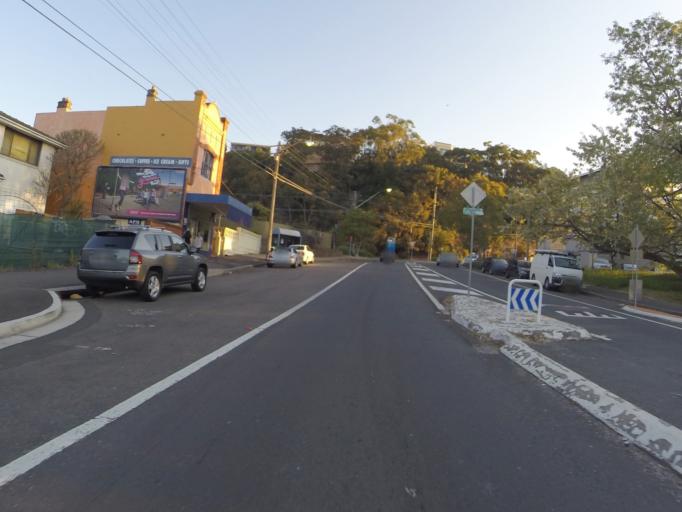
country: AU
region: New South Wales
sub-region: Rockdale
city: Bardwell Valley
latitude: -33.9229
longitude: 151.1427
